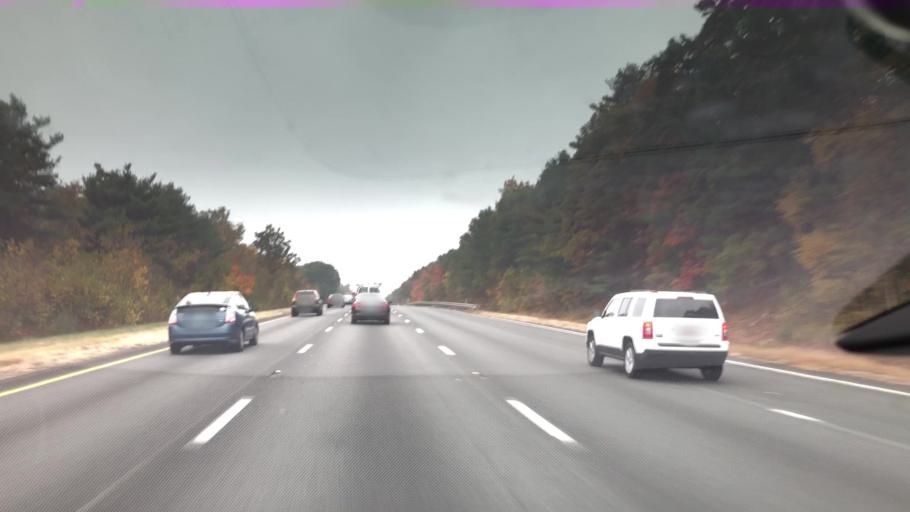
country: US
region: Massachusetts
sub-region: Middlesex County
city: Littleton Common
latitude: 42.5174
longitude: -71.5121
